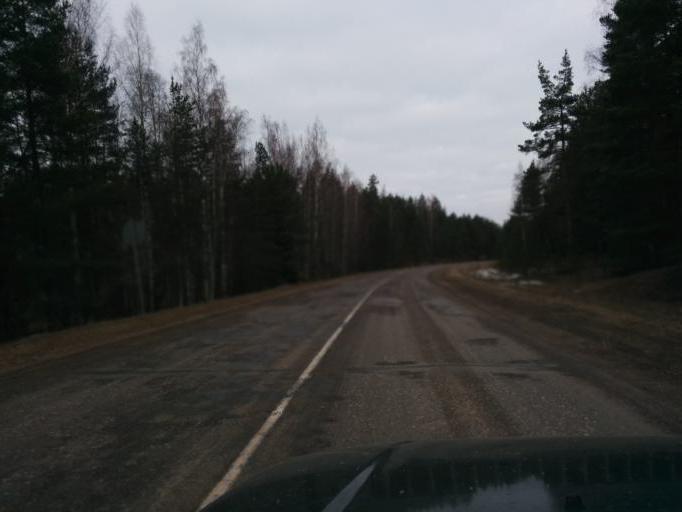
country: LV
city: Tireli
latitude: 56.8807
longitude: 23.5355
